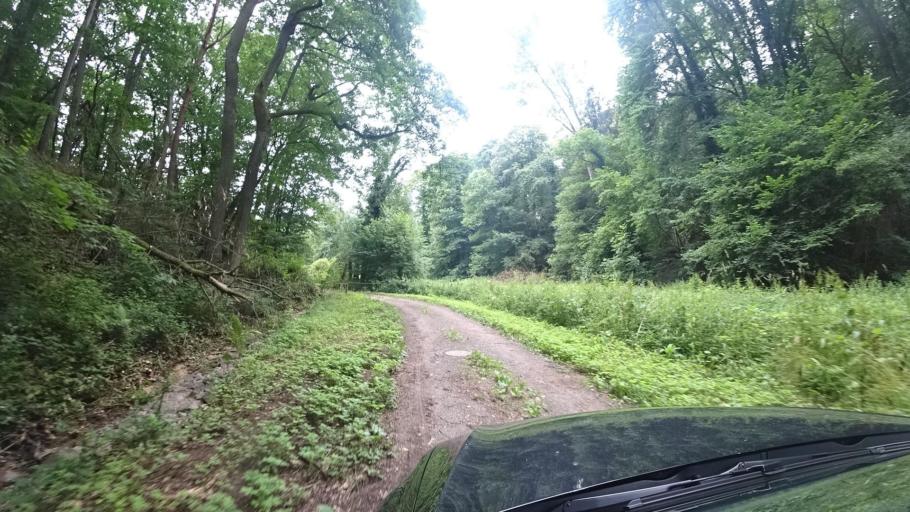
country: DE
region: Rheinland-Pfalz
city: Dorrenbach
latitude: 49.0904
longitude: 7.9772
